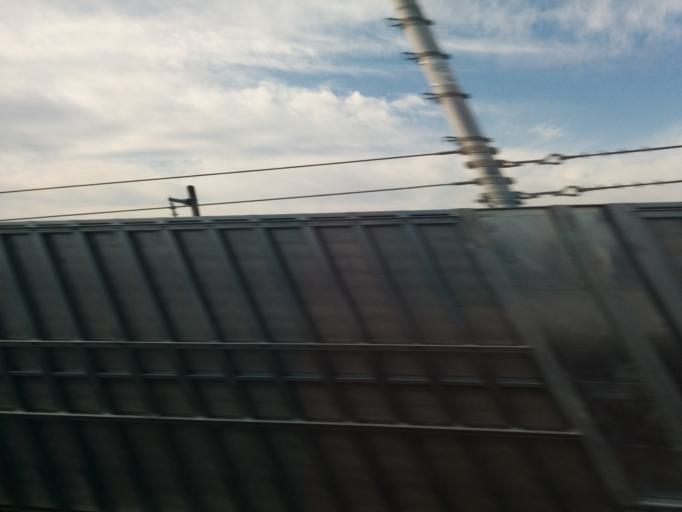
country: JP
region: Shiga Prefecture
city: Hikone
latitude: 35.2011
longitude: 136.2343
